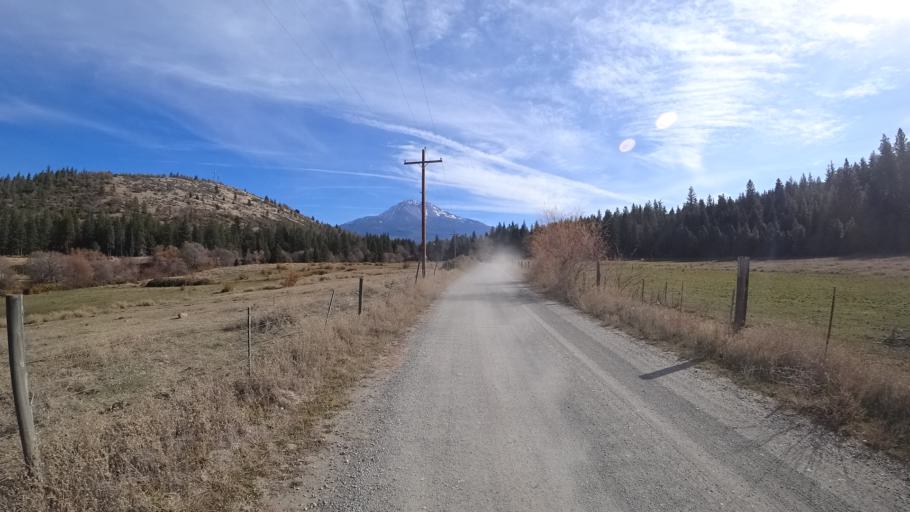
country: US
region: California
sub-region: Siskiyou County
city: Weed
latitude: 41.4324
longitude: -122.4066
